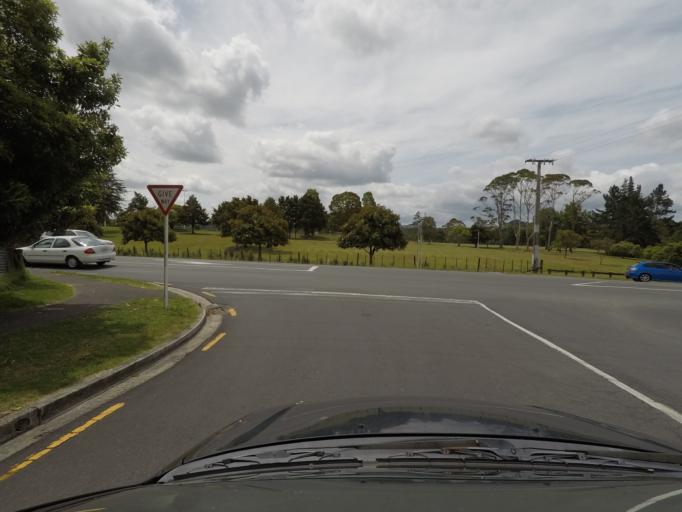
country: NZ
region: Northland
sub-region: Whangarei
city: Whangarei
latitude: -35.6839
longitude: 174.3342
